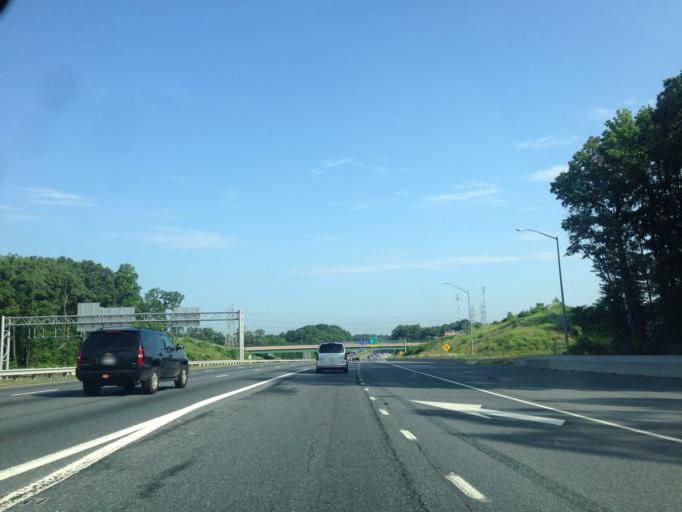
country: US
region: Maryland
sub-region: Baltimore County
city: Overlea
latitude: 39.3585
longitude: -76.5032
